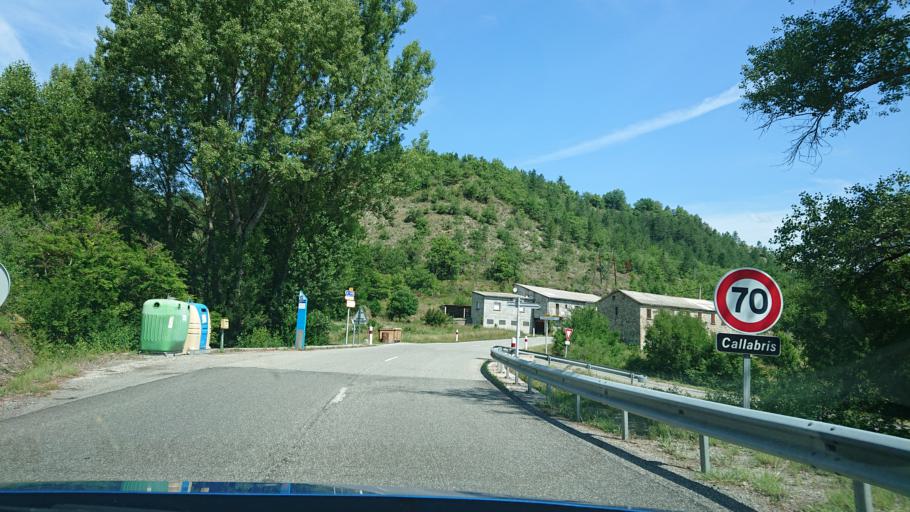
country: FR
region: Provence-Alpes-Cote d'Azur
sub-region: Departement des Alpes-de-Haute-Provence
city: Sisteron
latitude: 44.2766
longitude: 6.0105
